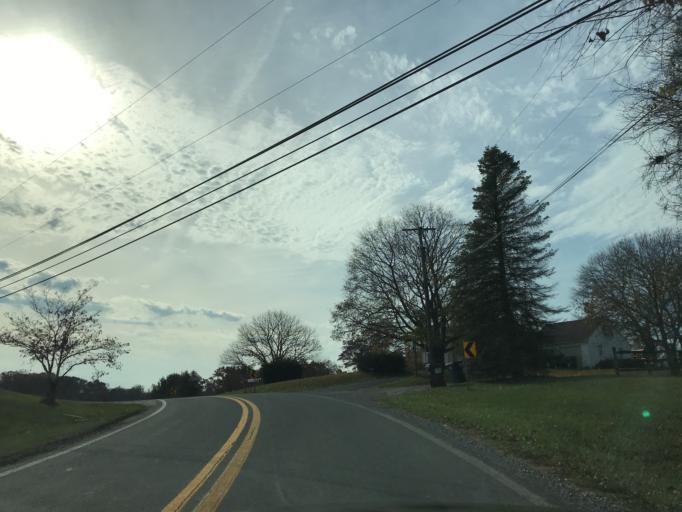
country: US
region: Maryland
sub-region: Carroll County
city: Eldersburg
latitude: 39.4560
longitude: -76.9155
